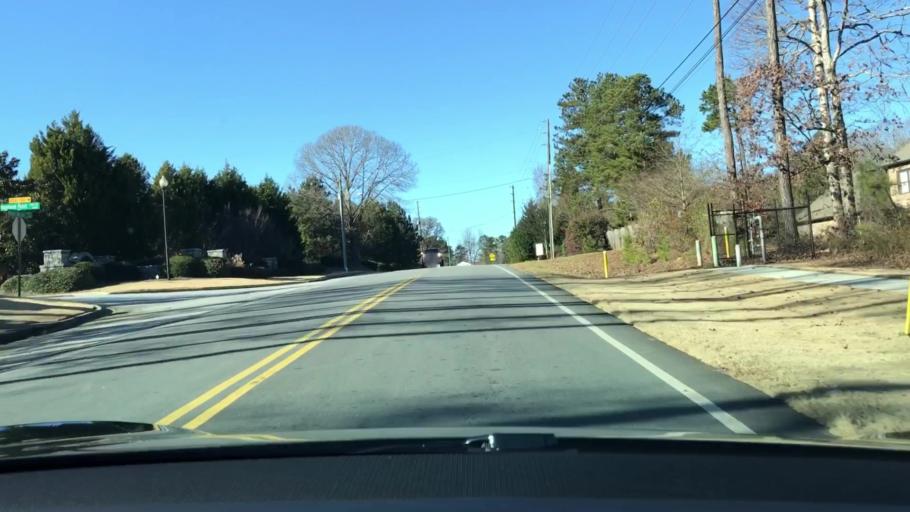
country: US
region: Georgia
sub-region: Barrow County
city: Auburn
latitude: 34.0688
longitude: -83.8554
